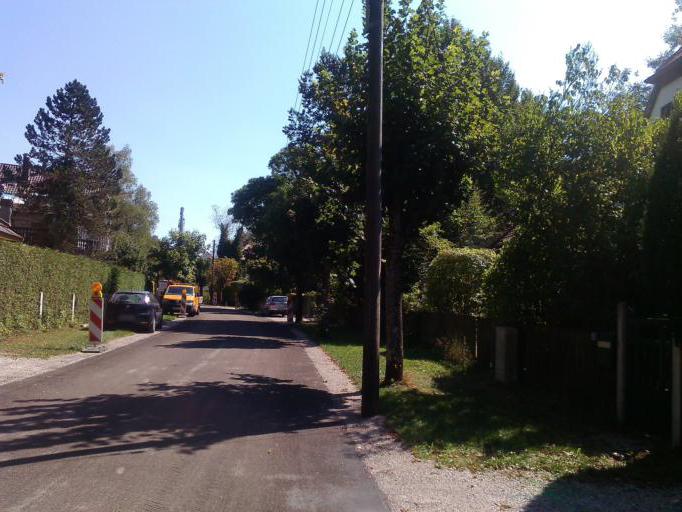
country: DE
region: Bavaria
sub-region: Upper Bavaria
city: Gauting
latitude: 48.0745
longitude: 11.3749
